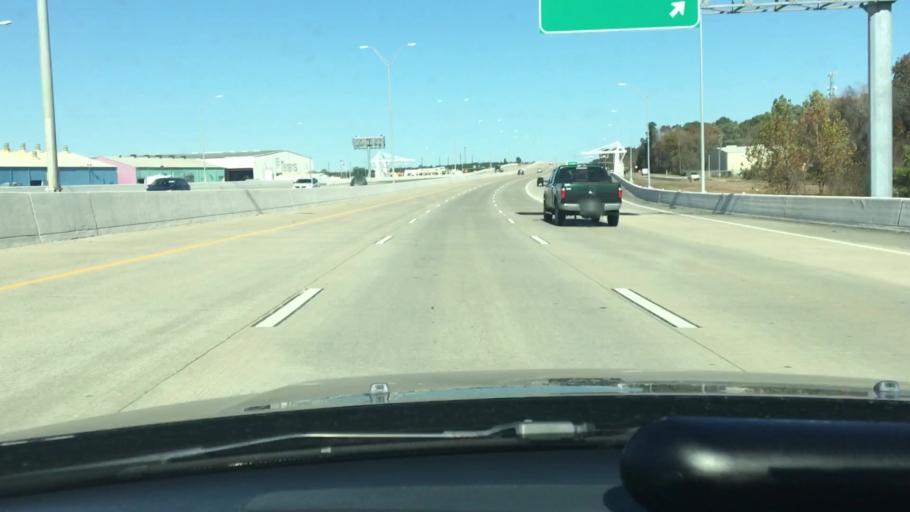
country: US
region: Texas
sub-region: Harris County
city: Sheldon
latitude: 29.8470
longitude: -95.1867
